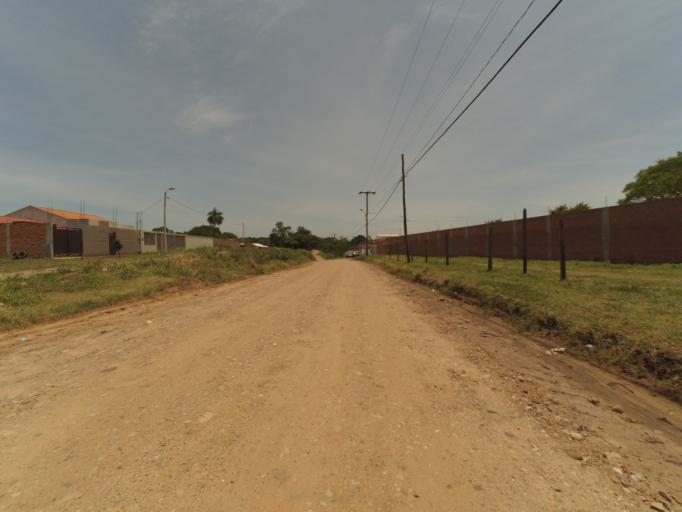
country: BO
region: Santa Cruz
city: Santa Cruz de la Sierra
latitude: -17.8400
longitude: -63.2446
